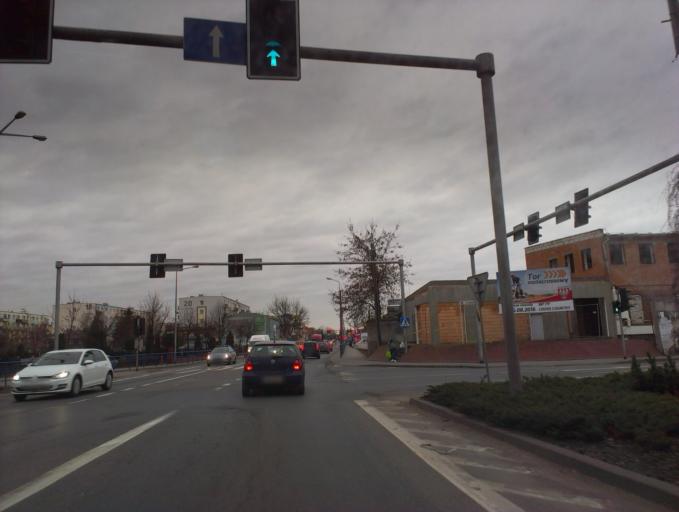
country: PL
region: Greater Poland Voivodeship
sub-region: Powiat obornicki
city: Oborniki
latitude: 52.6464
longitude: 16.8153
